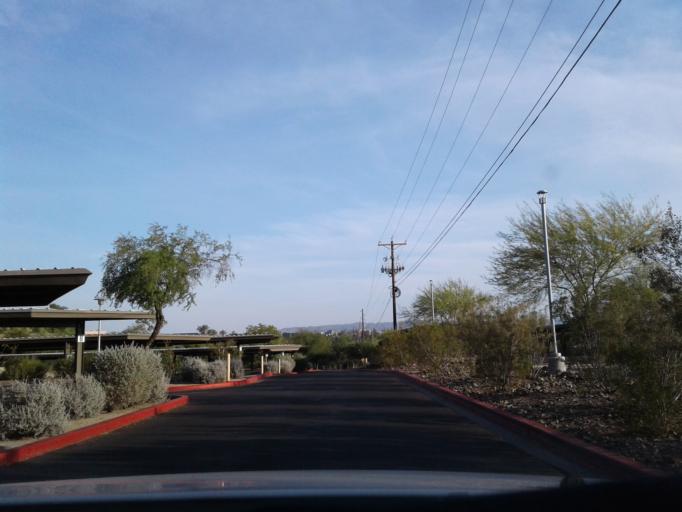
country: US
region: Arizona
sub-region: Maricopa County
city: Paradise Valley
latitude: 33.5288
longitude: -112.0302
